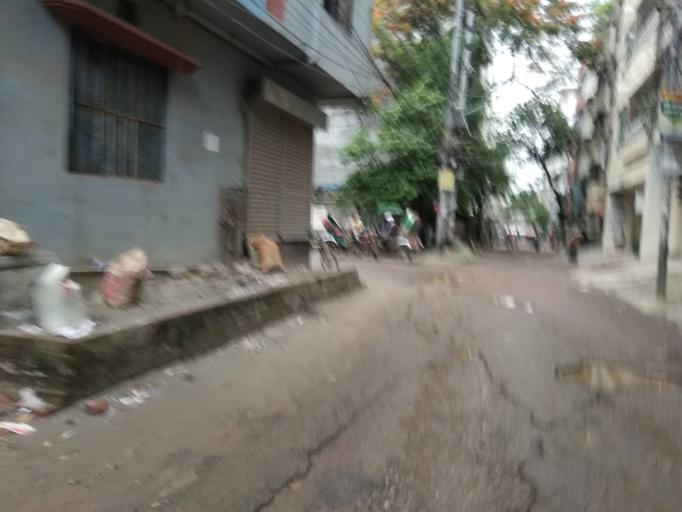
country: BD
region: Dhaka
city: Tungi
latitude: 23.8256
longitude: 90.3722
